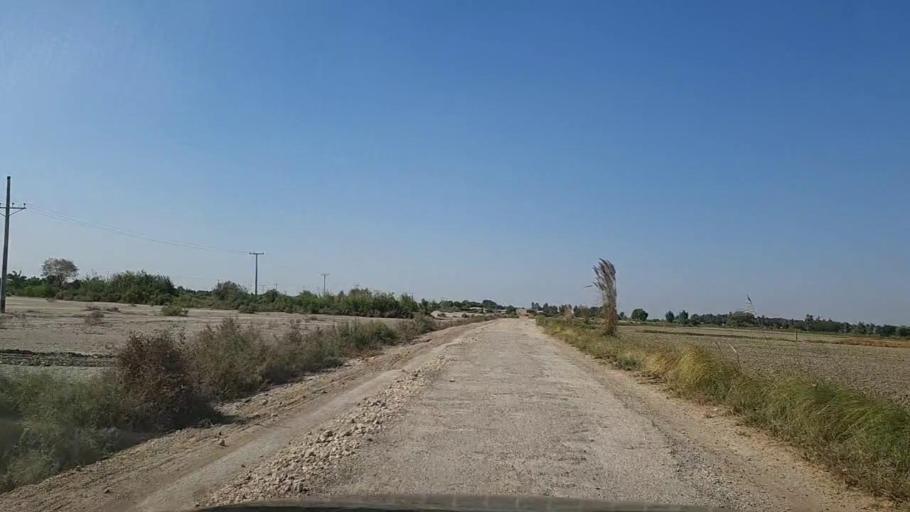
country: PK
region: Sindh
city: Mirpur Sakro
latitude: 24.6097
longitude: 67.7830
